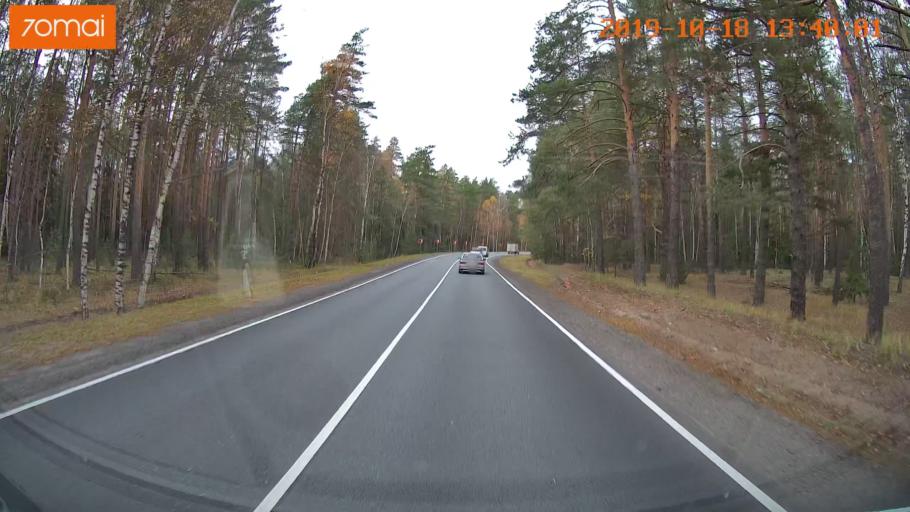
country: RU
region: Rjazan
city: Solotcha
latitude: 54.9050
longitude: 40.0016
